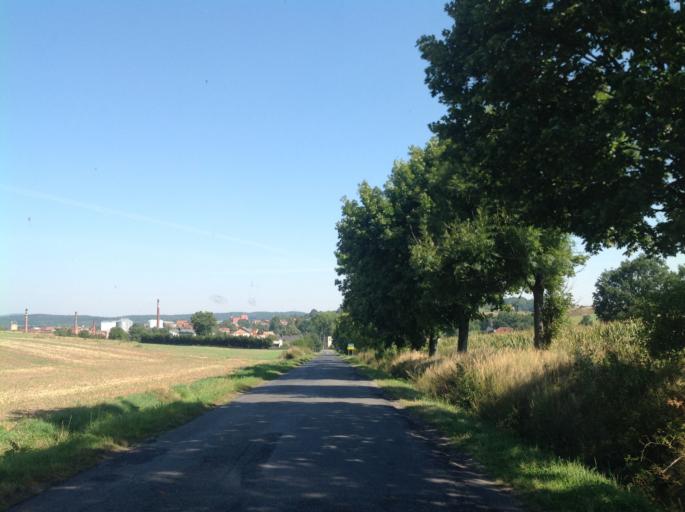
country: PL
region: Lower Silesian Voivodeship
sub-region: Powiat zabkowicki
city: Ziebice
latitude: 50.5850
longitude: 17.0242
